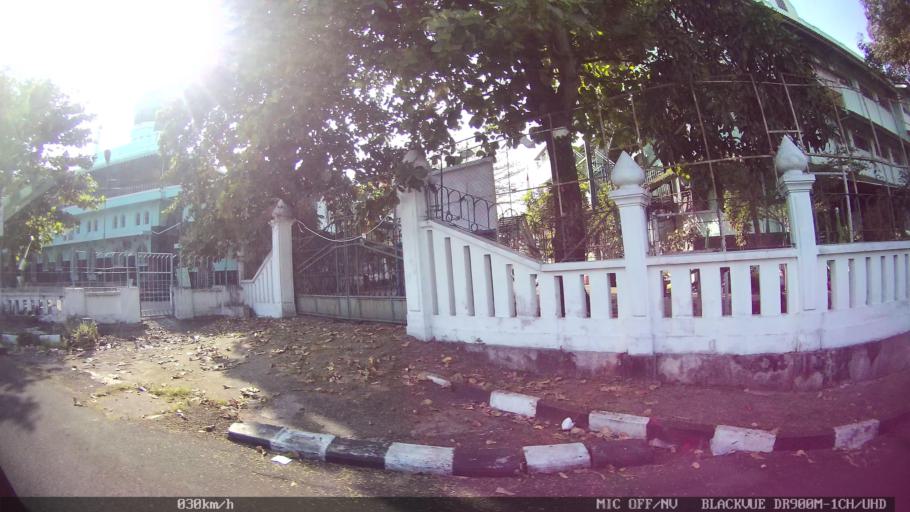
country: ID
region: Daerah Istimewa Yogyakarta
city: Yogyakarta
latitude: -7.7867
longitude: 110.3687
